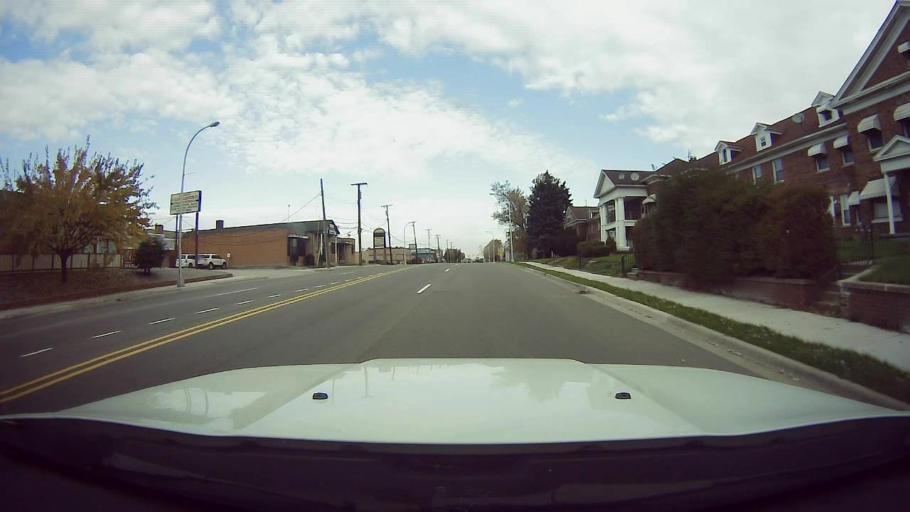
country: US
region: Michigan
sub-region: Wayne County
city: Dearborn
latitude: 42.3354
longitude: -83.1766
